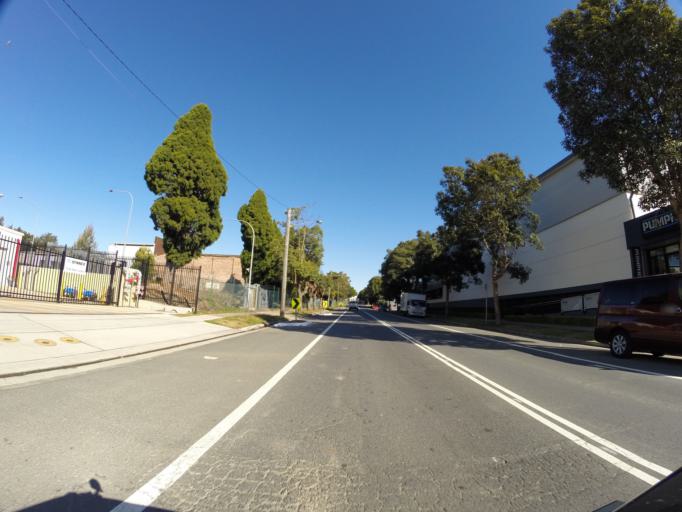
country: AU
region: New South Wales
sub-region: Auburn
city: Lidcombe
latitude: -33.8562
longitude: 151.0606
